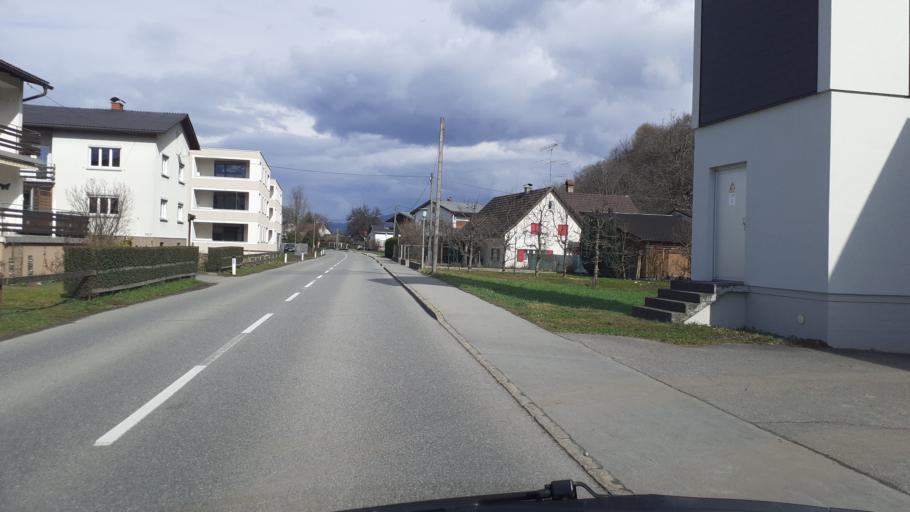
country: AT
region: Vorarlberg
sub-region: Politischer Bezirk Feldkirch
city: Koblach
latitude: 47.3435
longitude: 9.6058
